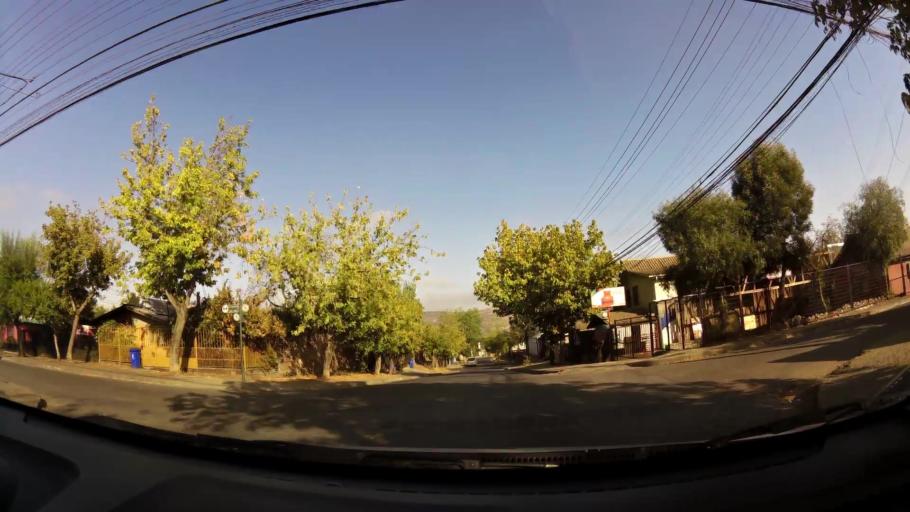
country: CL
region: Maule
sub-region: Provincia de Talca
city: Talca
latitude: -35.4086
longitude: -71.6549
